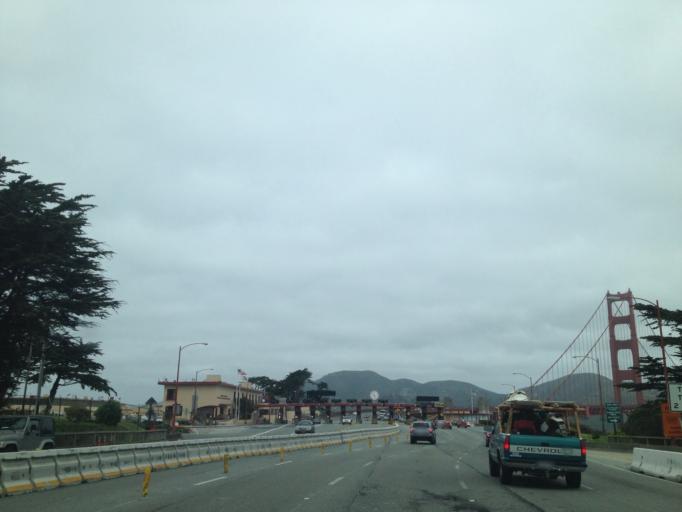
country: US
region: California
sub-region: Marin County
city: Sausalito
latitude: 37.8060
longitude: -122.4742
